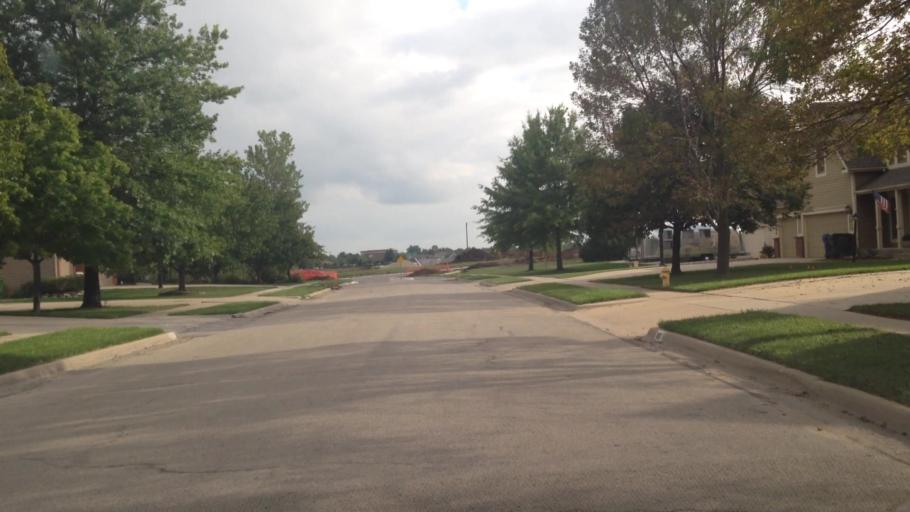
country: US
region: Kansas
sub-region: Douglas County
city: Lawrence
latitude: 38.9672
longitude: -95.3116
